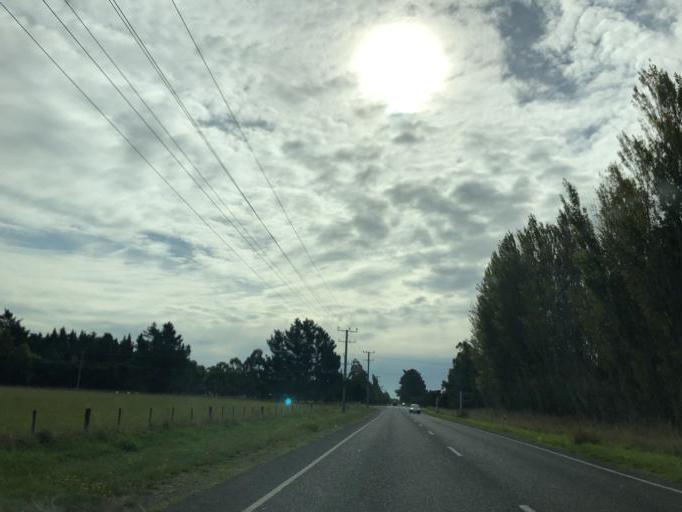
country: NZ
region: Canterbury
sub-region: Selwyn District
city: Rolleston
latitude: -43.6270
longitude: 172.4198
